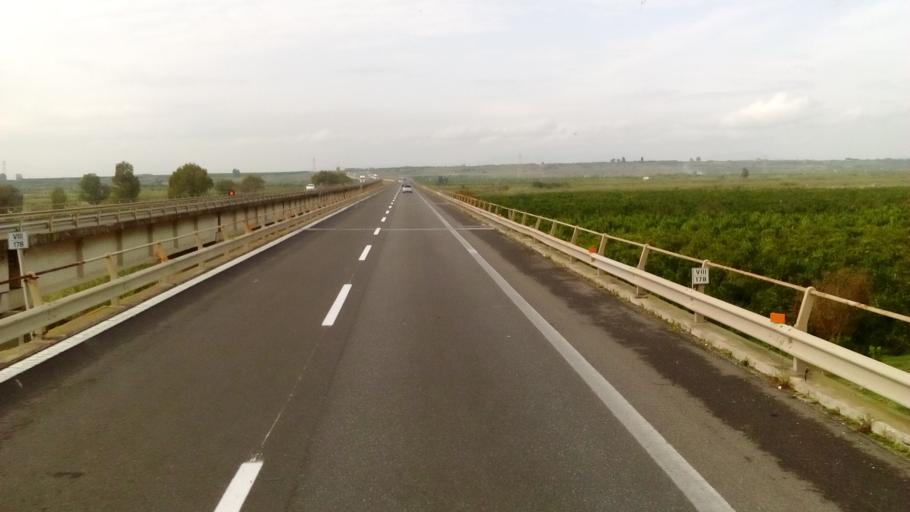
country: IT
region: Sicily
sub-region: Catania
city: Motta Sant'Anastasia
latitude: 37.4685
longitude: 14.8964
